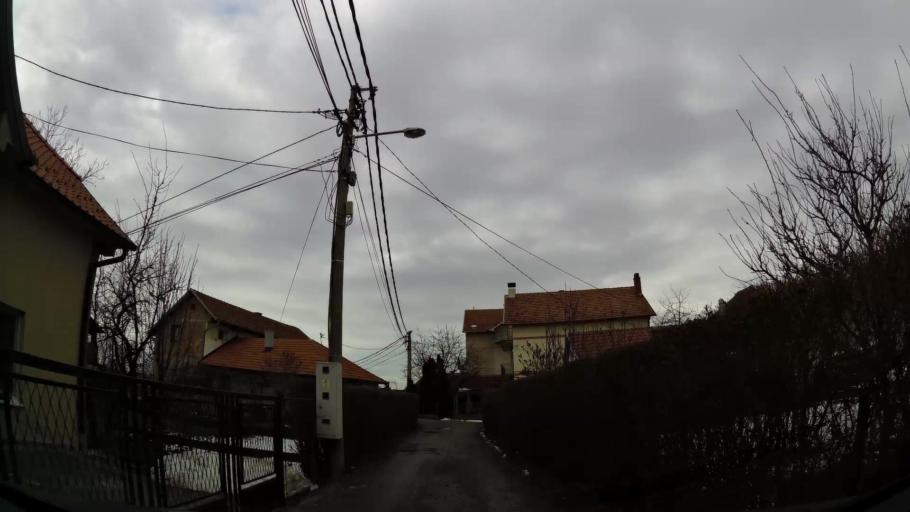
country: RS
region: Central Serbia
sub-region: Belgrade
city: Rakovica
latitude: 44.7433
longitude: 20.3955
